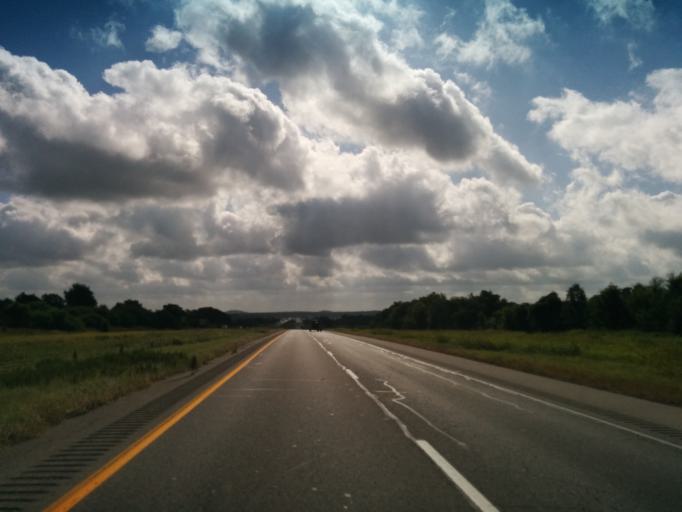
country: US
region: Texas
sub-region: Caldwell County
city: Luling
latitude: 29.6488
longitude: -97.6141
